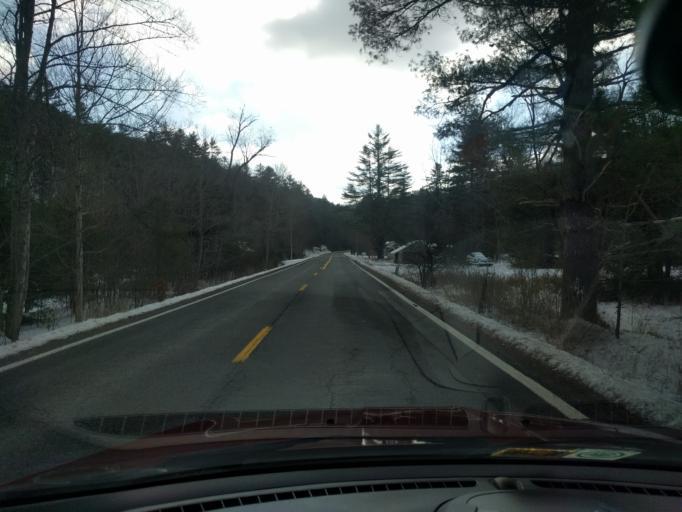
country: US
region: West Virginia
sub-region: Pocahontas County
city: Marlinton
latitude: 38.1438
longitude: -79.9783
